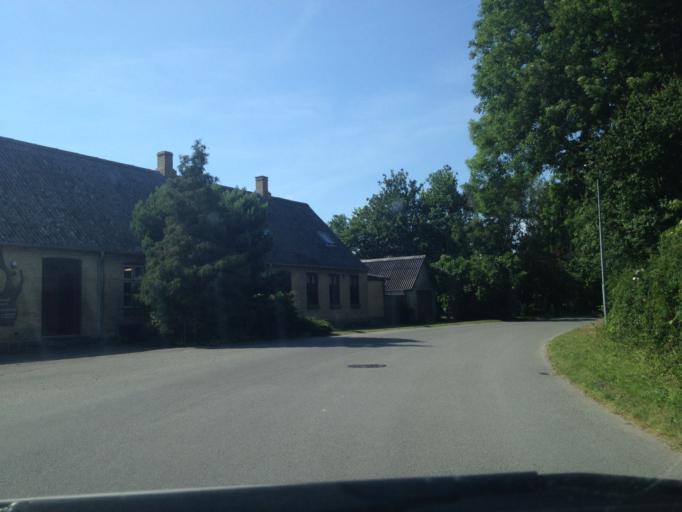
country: DK
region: Central Jutland
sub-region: Samso Kommune
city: Tranebjerg
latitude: 55.8130
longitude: 10.5551
